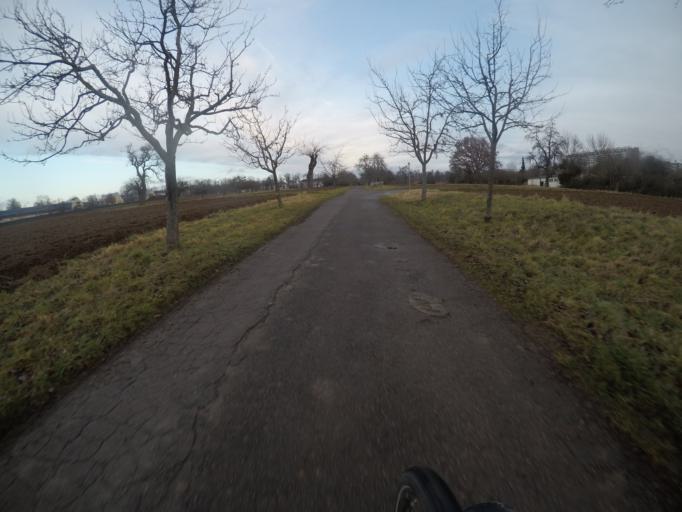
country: DE
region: Baden-Wuerttemberg
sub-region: Regierungsbezirk Stuttgart
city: Leinfelden-Echterdingen
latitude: 48.7217
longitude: 9.1863
